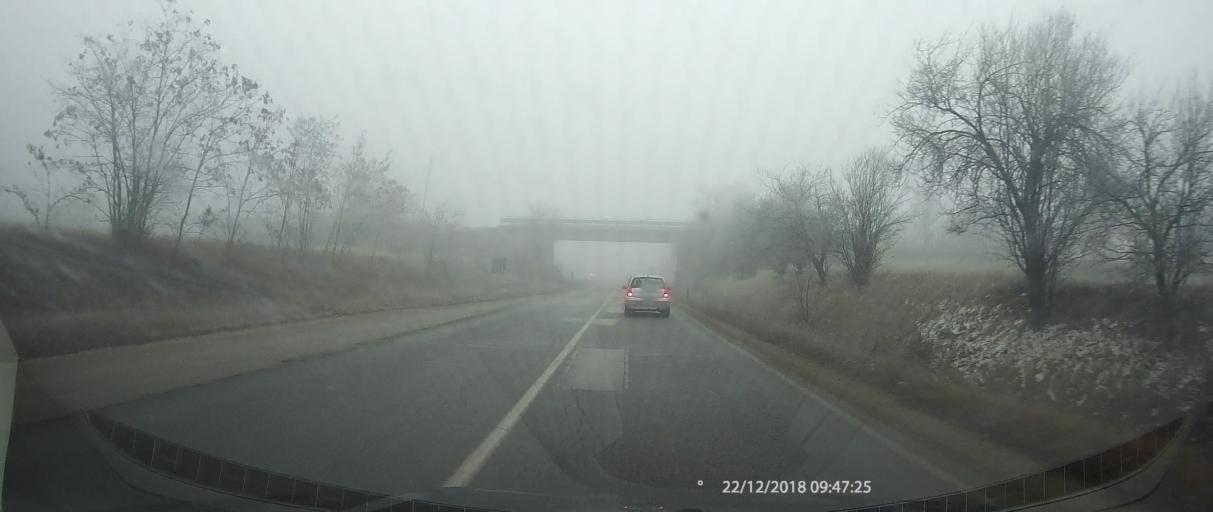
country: MK
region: Kumanovo
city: Kumanovo
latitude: 42.1623
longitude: 21.7392
